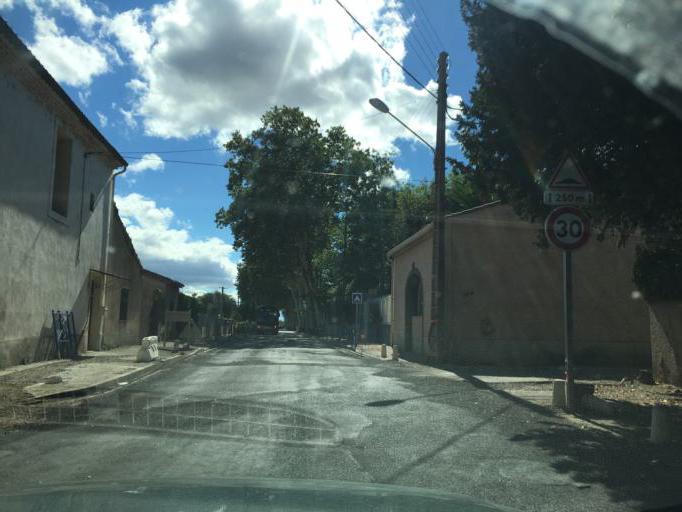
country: FR
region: Languedoc-Roussillon
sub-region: Departement de l'Herault
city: Pomerols
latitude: 43.3915
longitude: 3.4961
